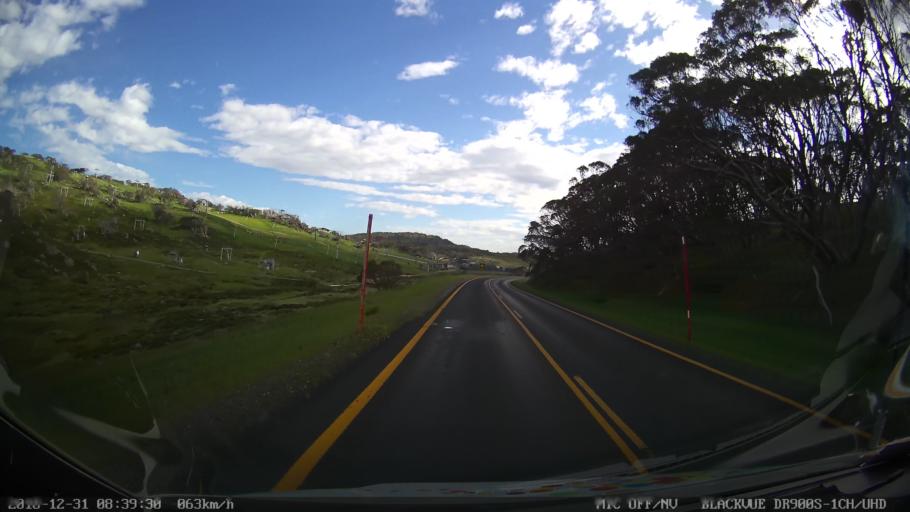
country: AU
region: New South Wales
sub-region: Snowy River
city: Jindabyne
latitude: -36.4084
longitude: 148.4067
